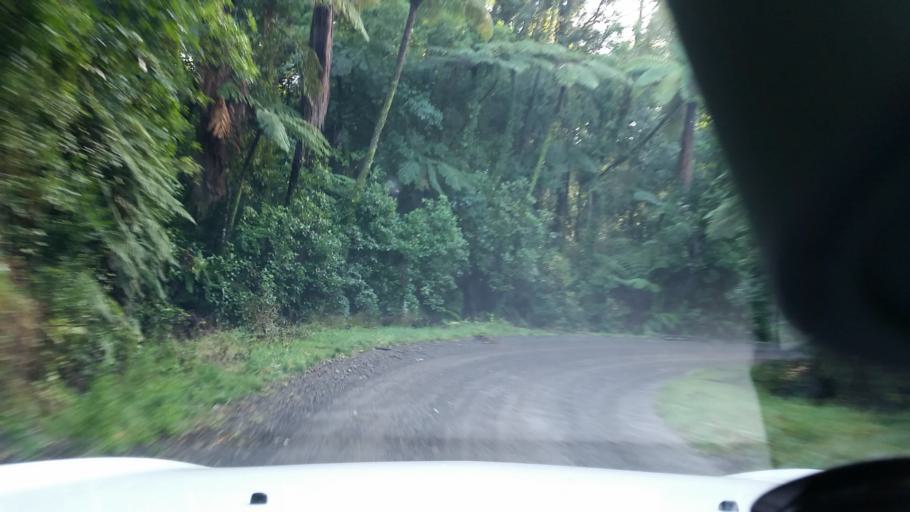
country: NZ
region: Bay of Plenty
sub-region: Kawerau District
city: Kawerau
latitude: -38.0210
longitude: 176.5752
